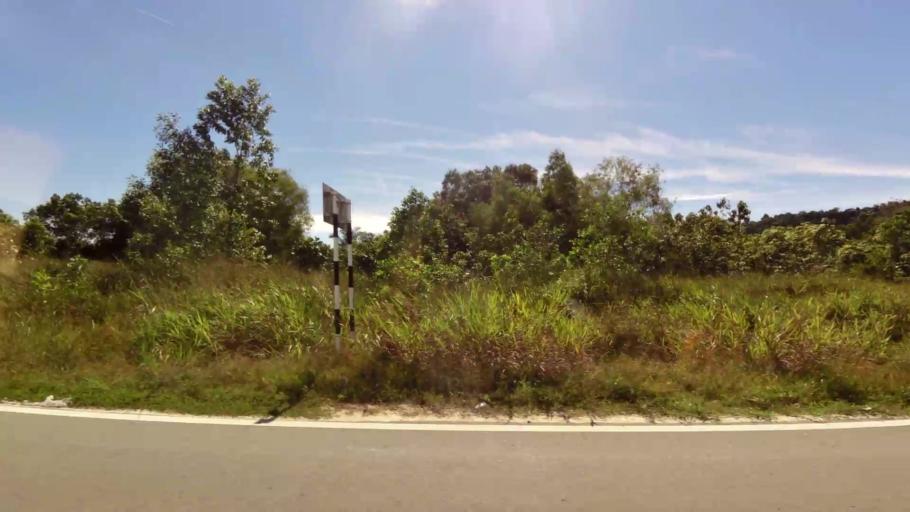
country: BN
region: Brunei and Muara
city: Bandar Seri Begawan
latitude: 5.0030
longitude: 115.0543
